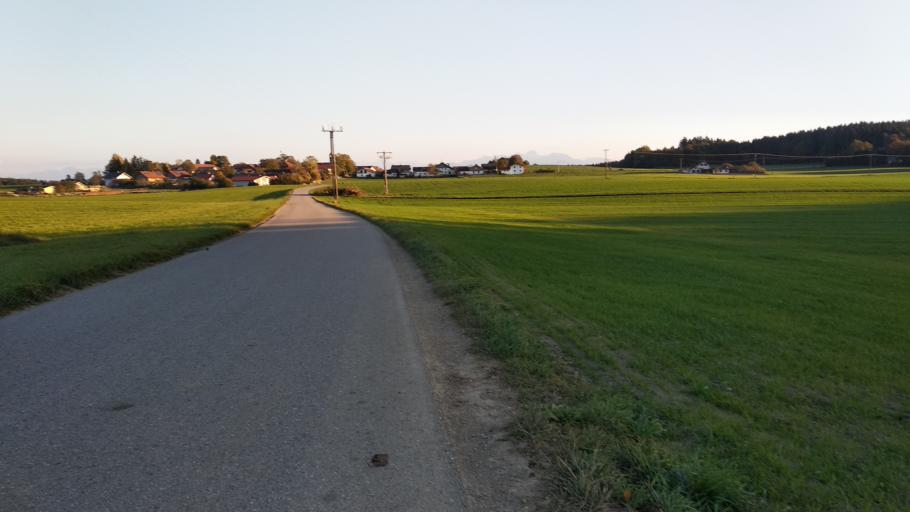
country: DE
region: Bavaria
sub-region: Upper Bavaria
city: Glonn
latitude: 47.9752
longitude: 11.8311
